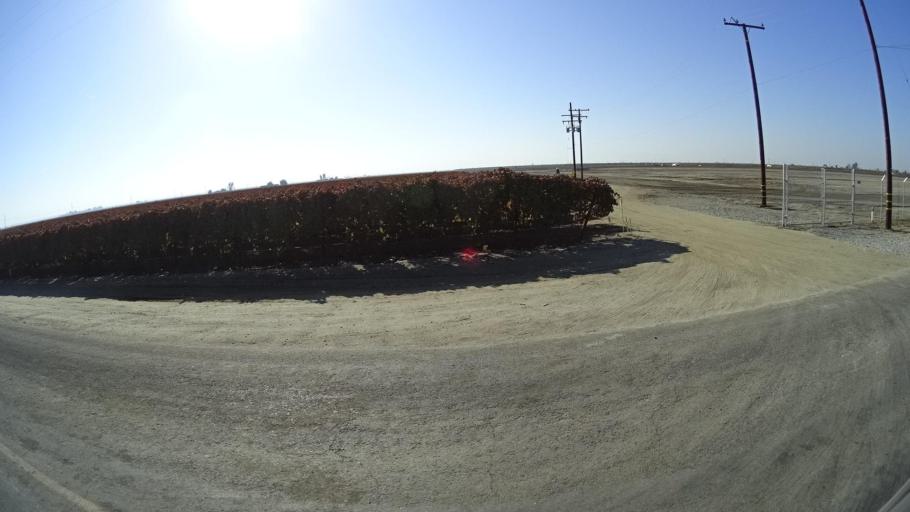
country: US
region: California
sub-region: Kern County
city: Delano
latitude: 35.7687
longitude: -119.2095
